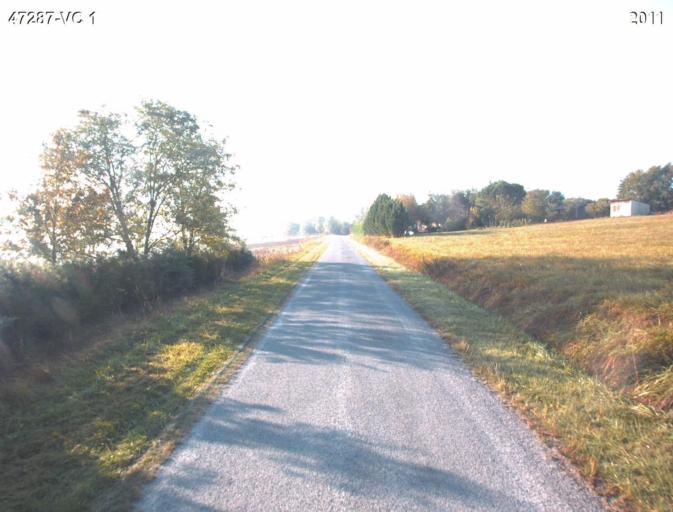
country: FR
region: Aquitaine
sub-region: Departement du Lot-et-Garonne
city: Sainte-Colombe-en-Bruilhois
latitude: 44.1388
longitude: 0.4468
